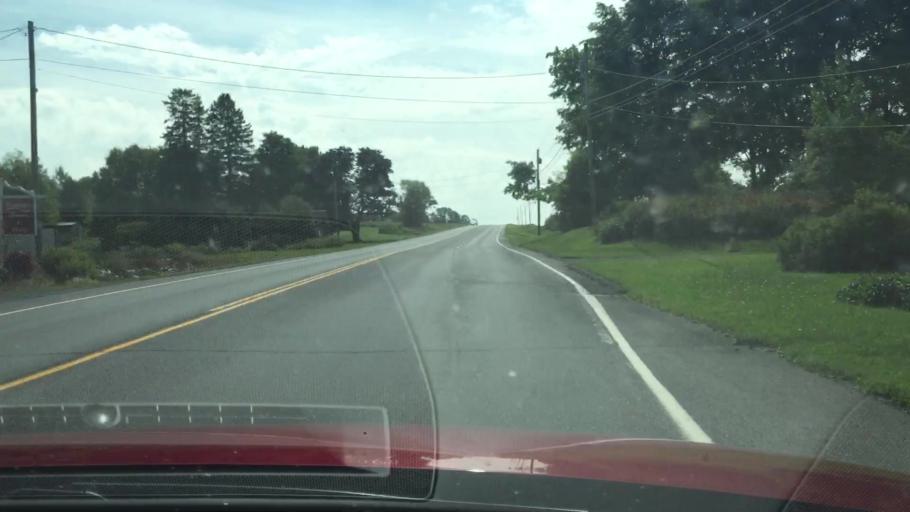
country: US
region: Maine
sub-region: Aroostook County
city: Easton
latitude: 46.5823
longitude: -67.9582
